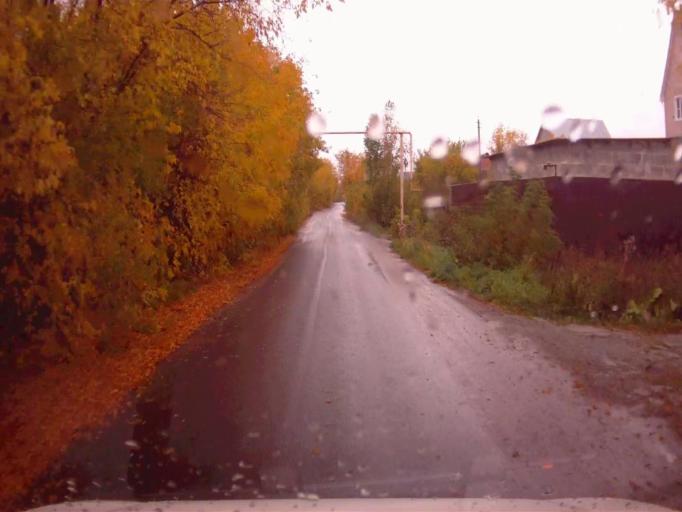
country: RU
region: Chelyabinsk
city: Dolgoderevenskoye
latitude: 55.3032
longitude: 61.3374
